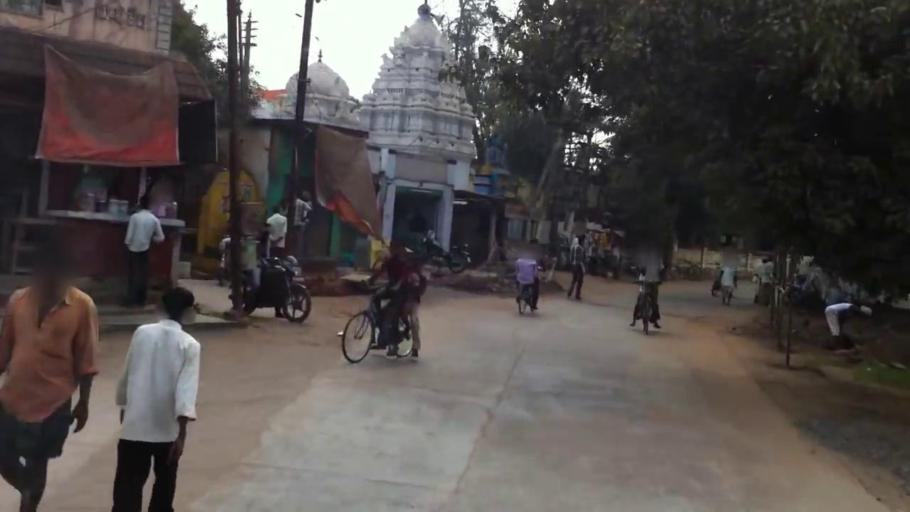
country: IN
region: Andhra Pradesh
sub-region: Guntur
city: Bhattiprolu
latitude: 16.2278
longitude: 80.6525
